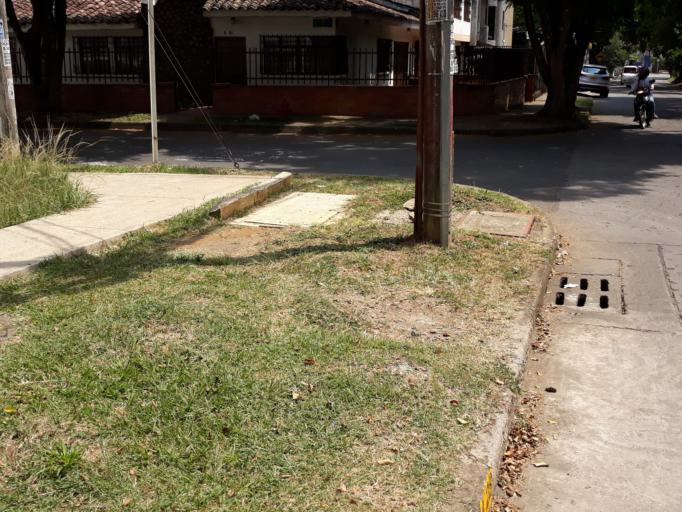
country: CO
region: Valle del Cauca
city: Cali
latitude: 3.3795
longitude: -76.5413
